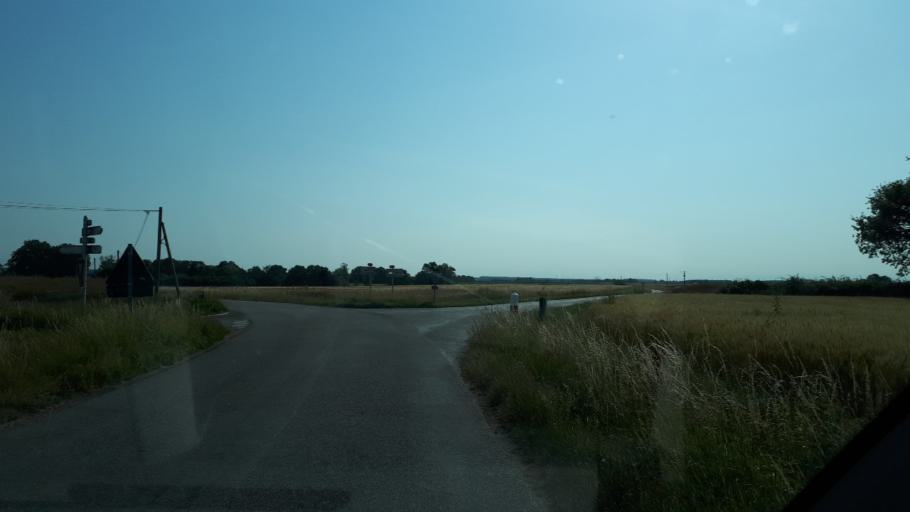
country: FR
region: Centre
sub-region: Departement d'Eure-et-Loir
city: Arrou
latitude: 48.0686
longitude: 1.1118
